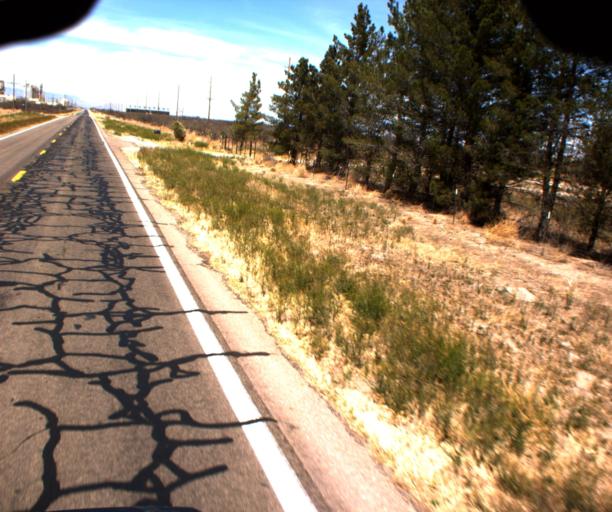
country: US
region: Arizona
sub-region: Cochise County
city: Willcox
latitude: 32.0490
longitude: -109.8855
